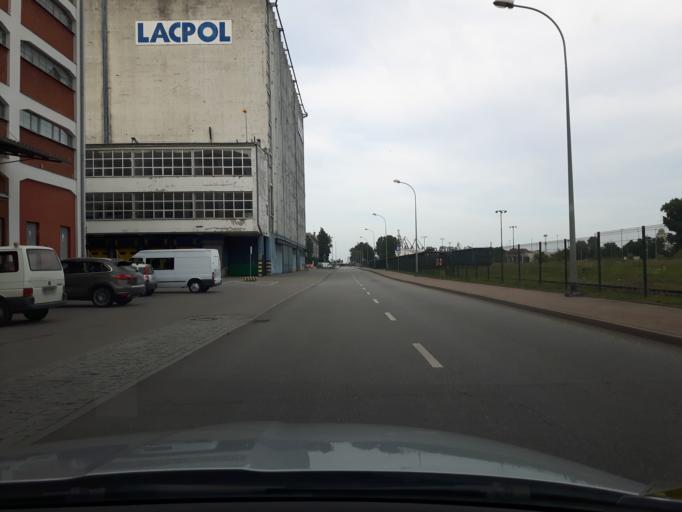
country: PL
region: Pomeranian Voivodeship
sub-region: Gdynia
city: Gdynia
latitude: 54.5284
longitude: 18.5349
